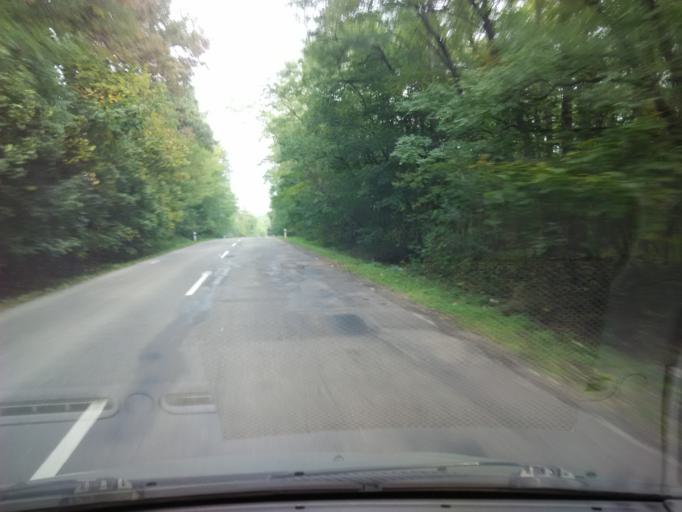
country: SK
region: Nitriansky
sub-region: Okres Nove Zamky
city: Nove Zamky
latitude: 47.9600
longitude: 18.2518
